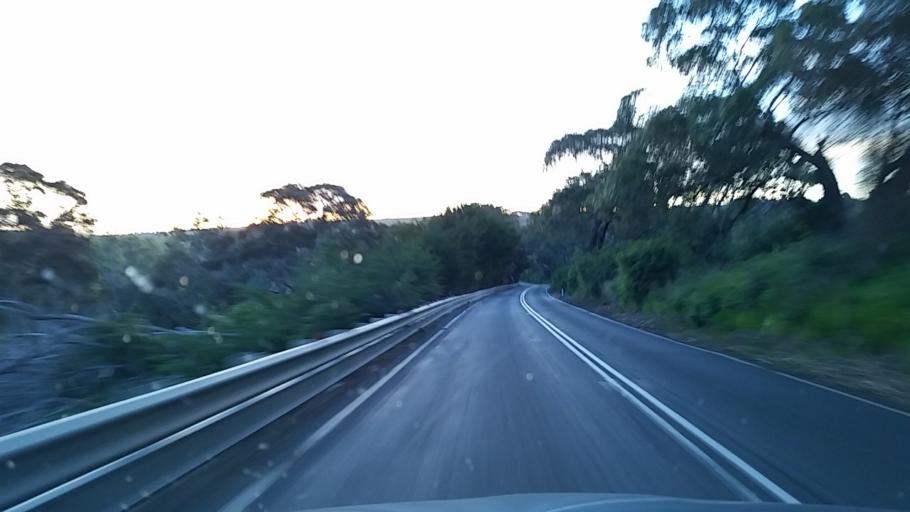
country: AU
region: South Australia
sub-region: Yankalilla
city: Normanville
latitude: -35.4226
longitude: 138.4095
